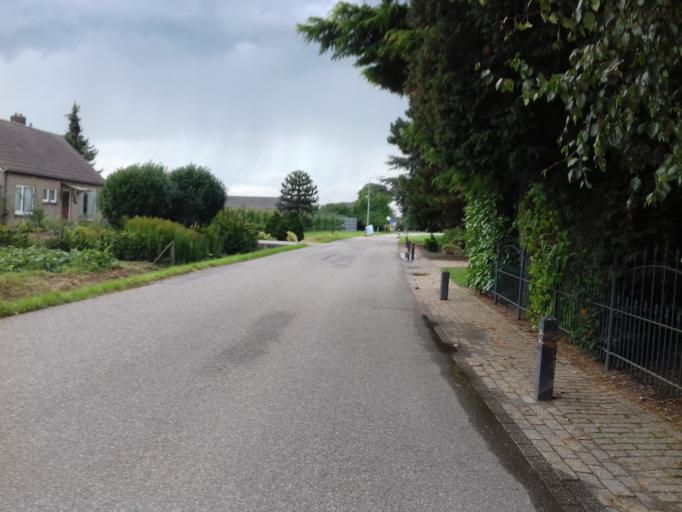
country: NL
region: Gelderland
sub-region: Gemeente Geldermalsen
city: Geldermalsen
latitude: 51.8883
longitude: 5.2615
